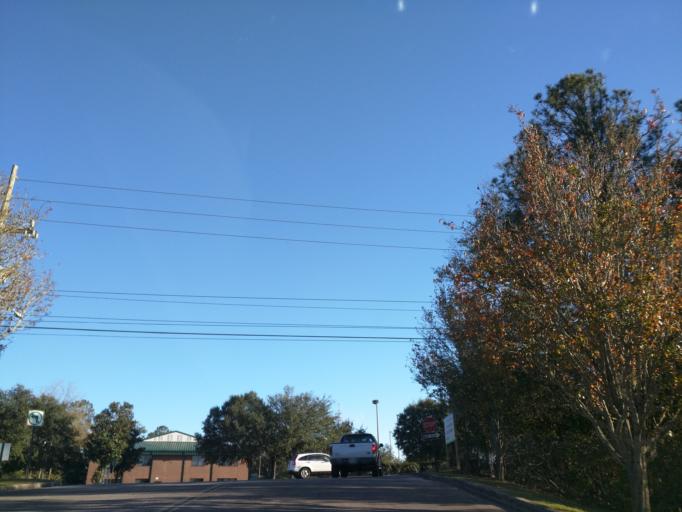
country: US
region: Florida
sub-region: Leon County
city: Tallahassee
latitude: 30.4732
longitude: -84.2904
